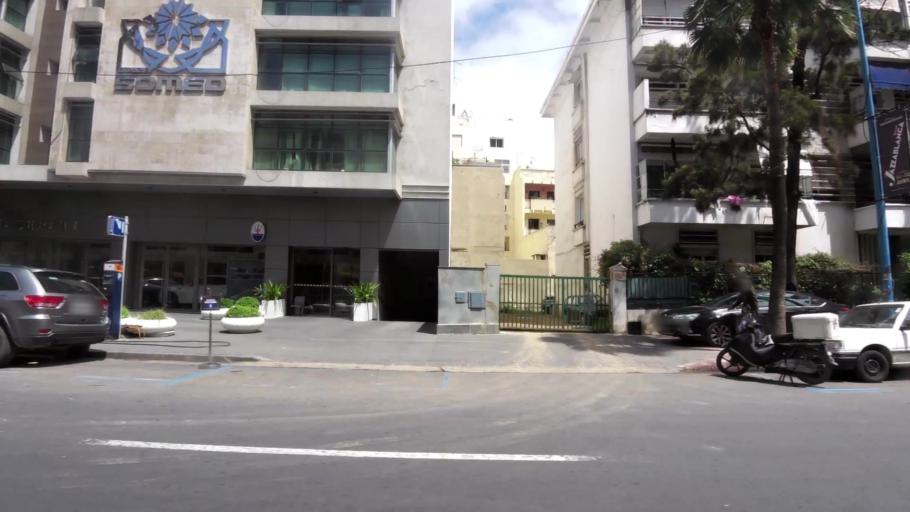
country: MA
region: Grand Casablanca
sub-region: Casablanca
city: Casablanca
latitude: 33.5918
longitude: -7.6365
